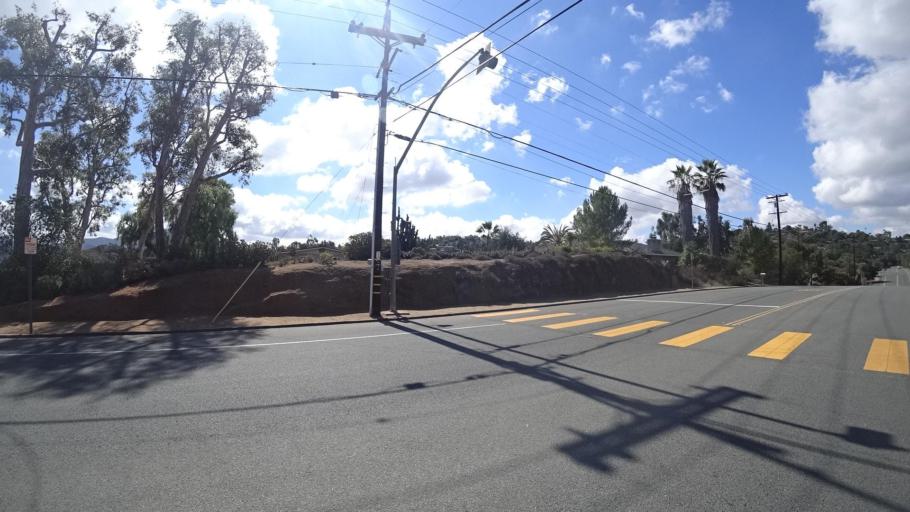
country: US
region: California
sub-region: San Diego County
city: Rancho San Diego
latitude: 32.7622
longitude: -116.9482
